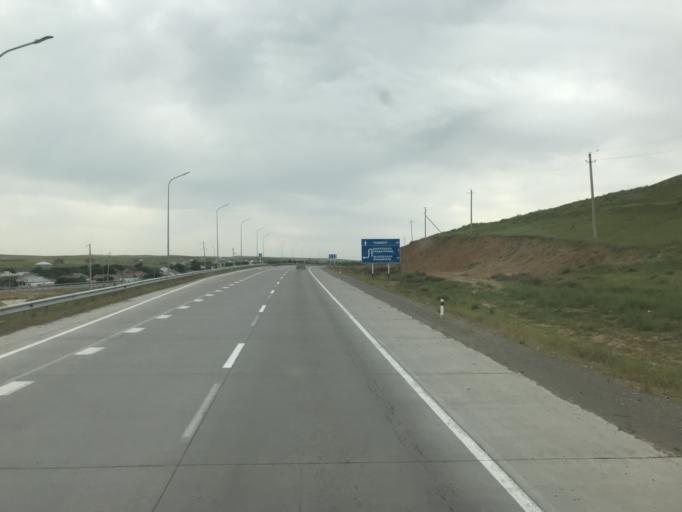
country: KZ
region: Ongtustik Qazaqstan
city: Qazyqurt
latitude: 41.8988
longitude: 69.4542
